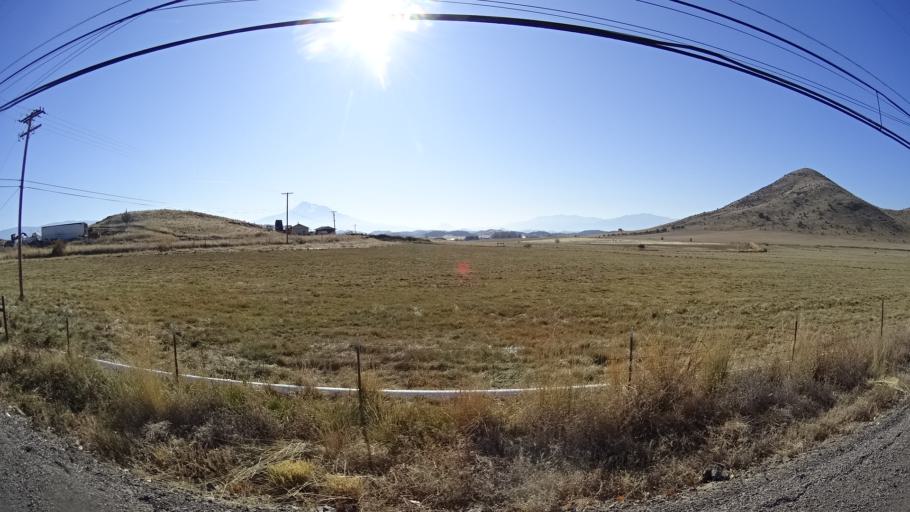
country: US
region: California
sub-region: Siskiyou County
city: Montague
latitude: 41.7255
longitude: -122.5066
